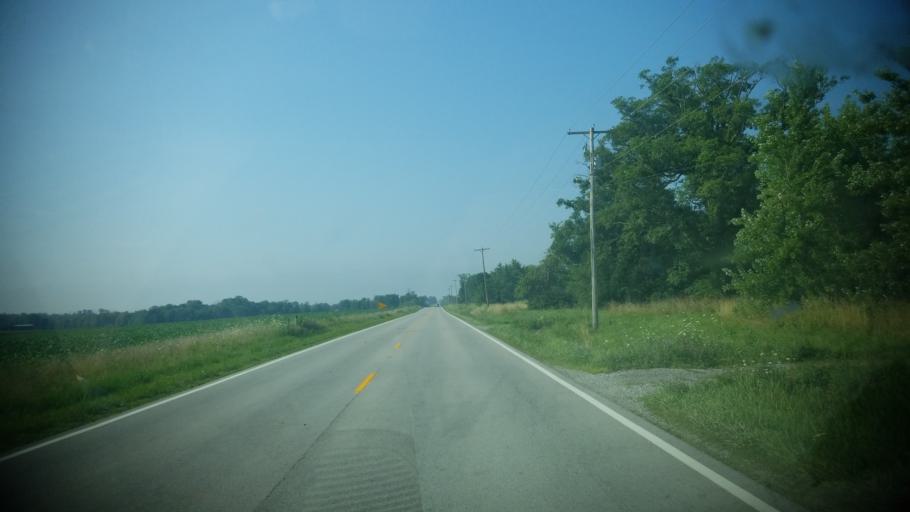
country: US
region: Illinois
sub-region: Clay County
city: Flora
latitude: 38.6029
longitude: -88.4385
